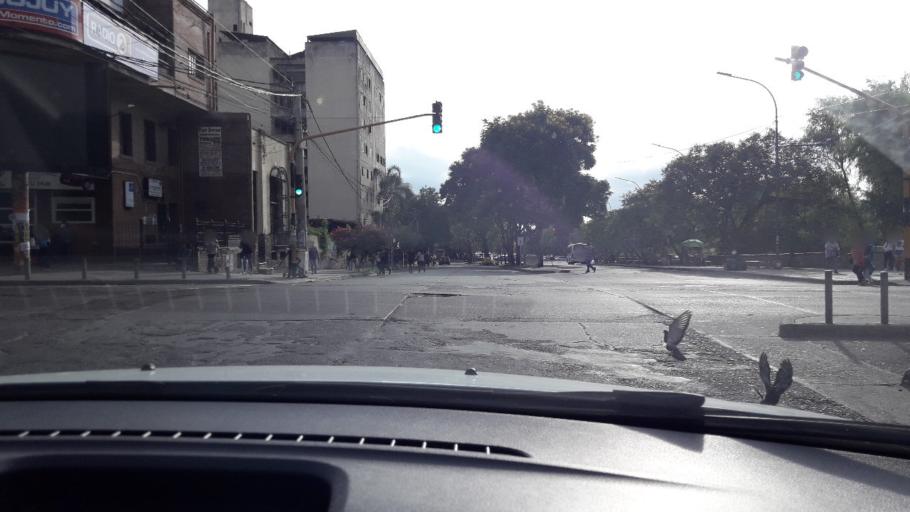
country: AR
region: Jujuy
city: San Salvador de Jujuy
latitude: -24.1889
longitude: -65.3028
